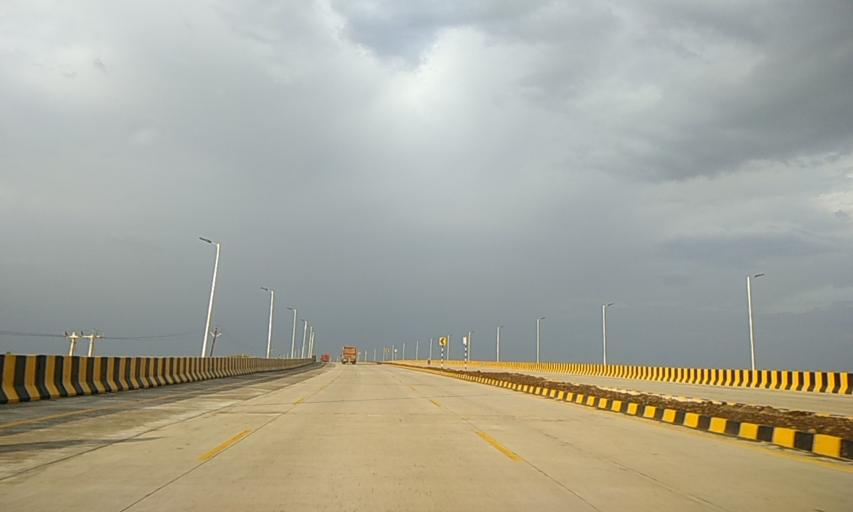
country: IN
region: Madhya Pradesh
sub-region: Rajgarh
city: Sarangpur
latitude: 23.5569
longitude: 76.4828
